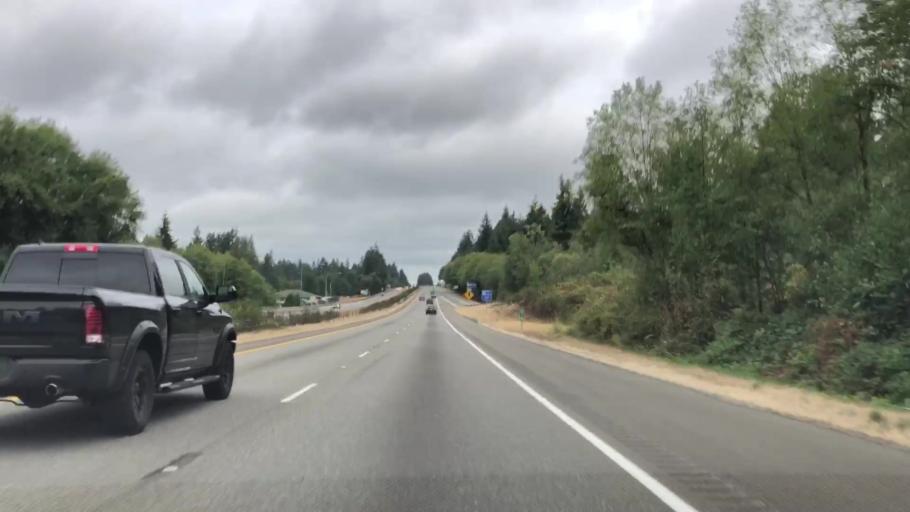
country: US
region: Washington
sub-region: Pierce County
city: Canterwood
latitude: 47.3600
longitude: -122.6150
